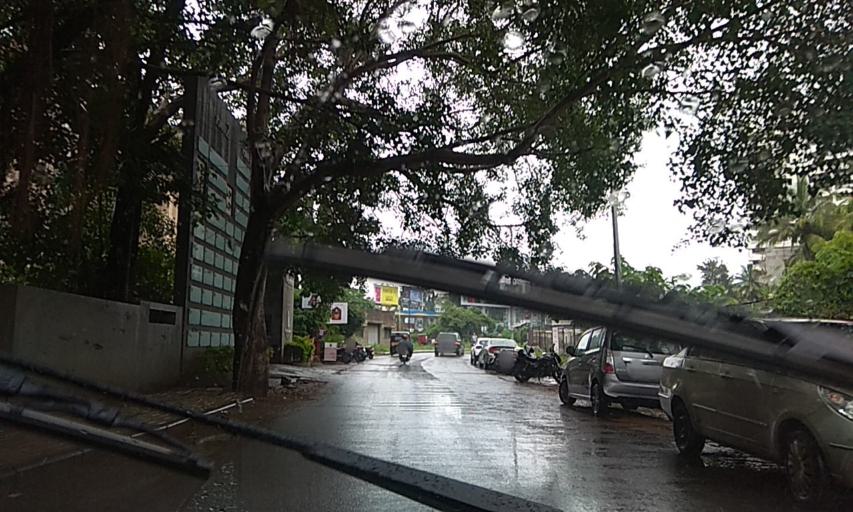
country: IN
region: Maharashtra
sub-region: Pune Division
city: Khadki
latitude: 18.5565
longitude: 73.7991
